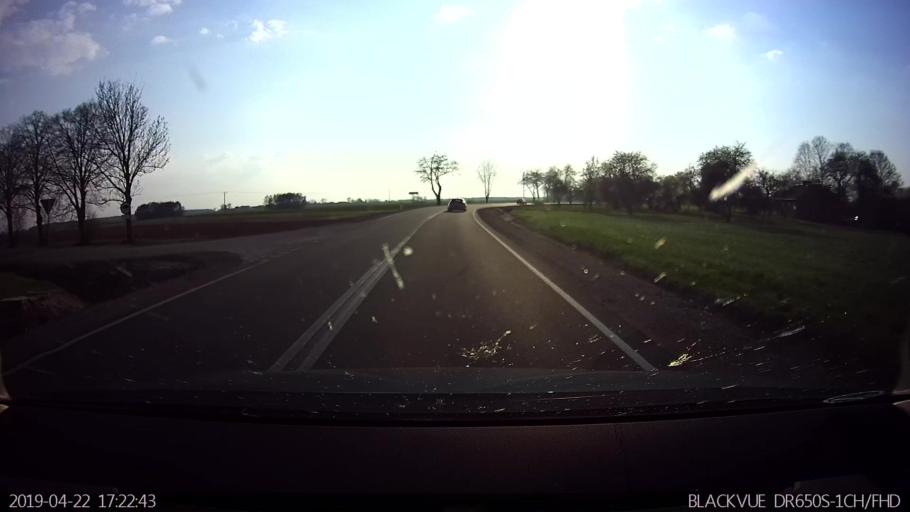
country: PL
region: Masovian Voivodeship
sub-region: Powiat sokolowski
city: Repki
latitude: 52.3896
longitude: 22.3330
